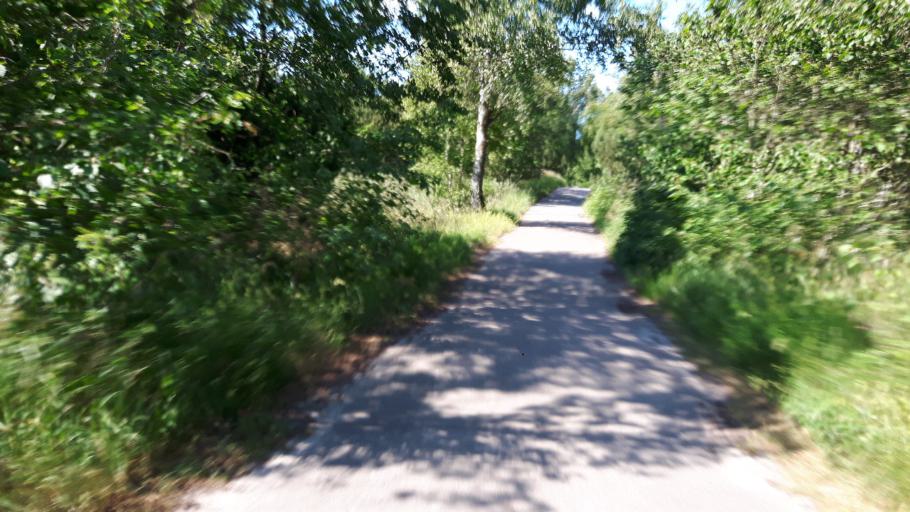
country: LT
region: Klaipedos apskritis
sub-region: Klaipeda
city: Klaipeda
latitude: 55.6869
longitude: 21.1038
